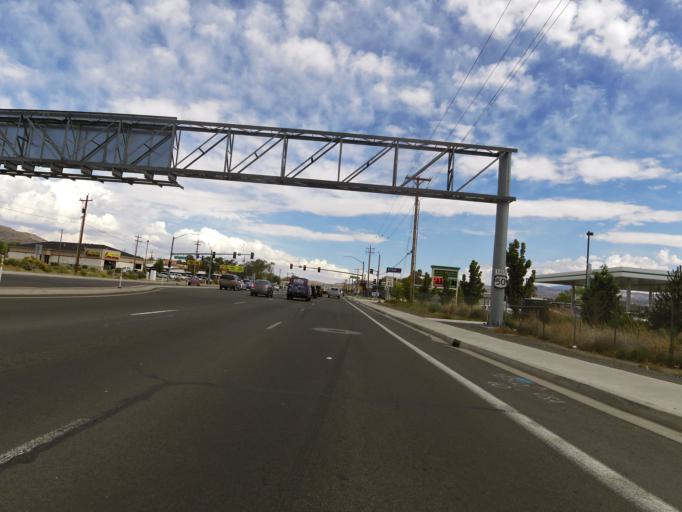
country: US
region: Nevada
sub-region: Carson City
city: Carson City
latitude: 39.1750
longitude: -119.7393
